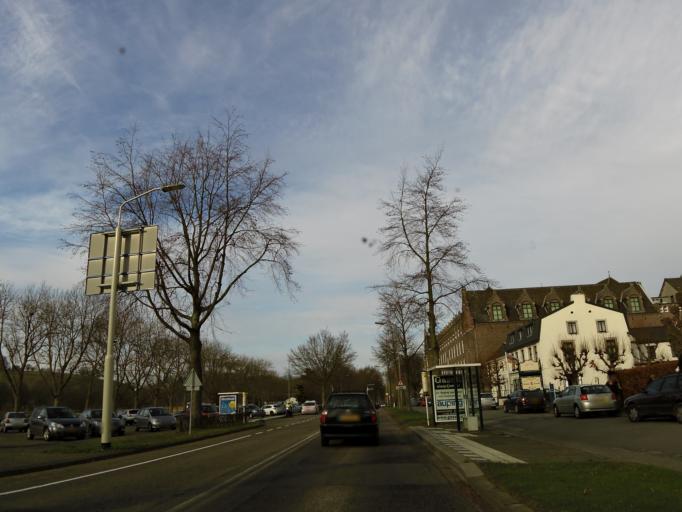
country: NL
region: Limburg
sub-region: Gemeente Voerendaal
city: Ubachsberg
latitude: 50.8128
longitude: 5.9135
